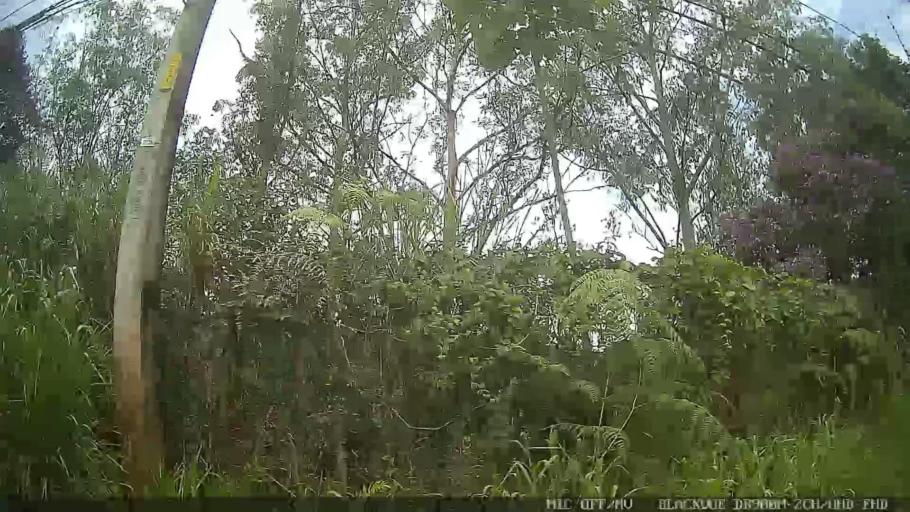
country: BR
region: Sao Paulo
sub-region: Santa Isabel
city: Santa Isabel
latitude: -23.3534
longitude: -46.2369
